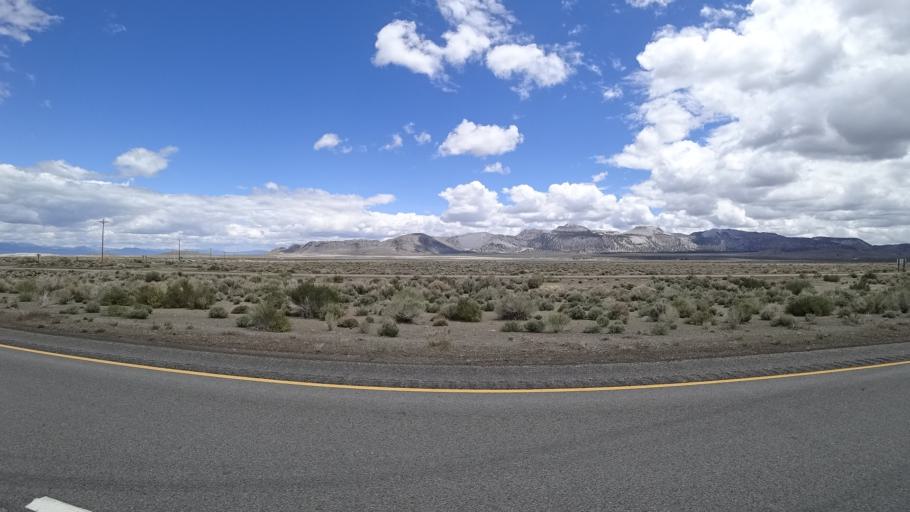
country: US
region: California
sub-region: Mono County
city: Mammoth Lakes
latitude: 37.8857
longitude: -119.0911
